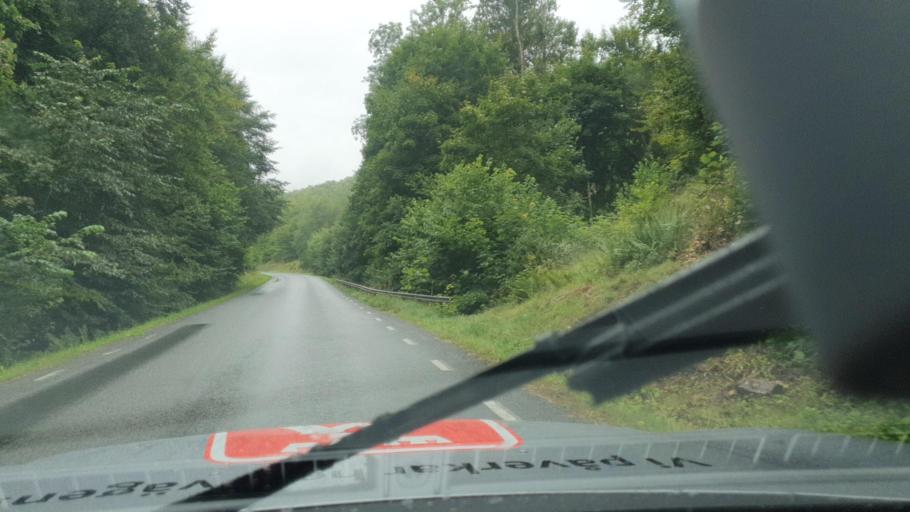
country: SE
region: Skane
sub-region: Hassleholms Kommun
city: Vinslov
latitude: 56.0849
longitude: 13.8443
